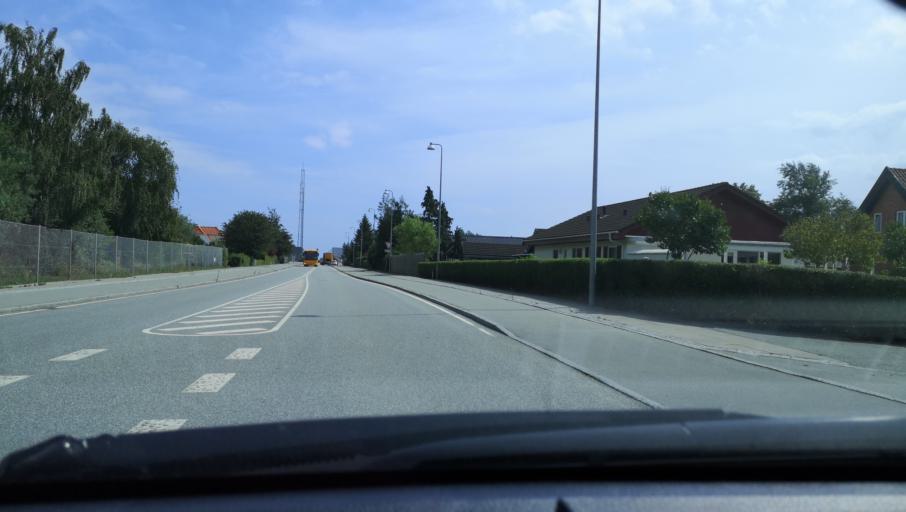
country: DK
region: Zealand
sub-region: Solrod Kommune
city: Solrod
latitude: 55.4998
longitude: 12.1919
